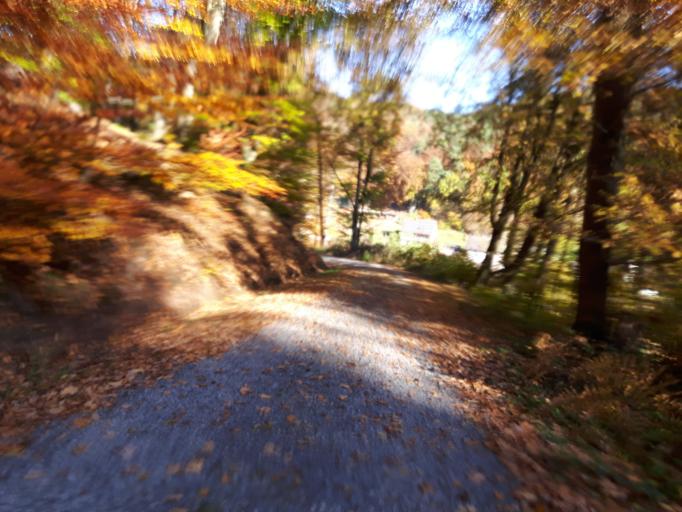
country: DE
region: Bavaria
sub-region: Regierungsbezirk Unterfranken
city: Heimbuchenthal
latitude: 49.8974
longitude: 9.3026
